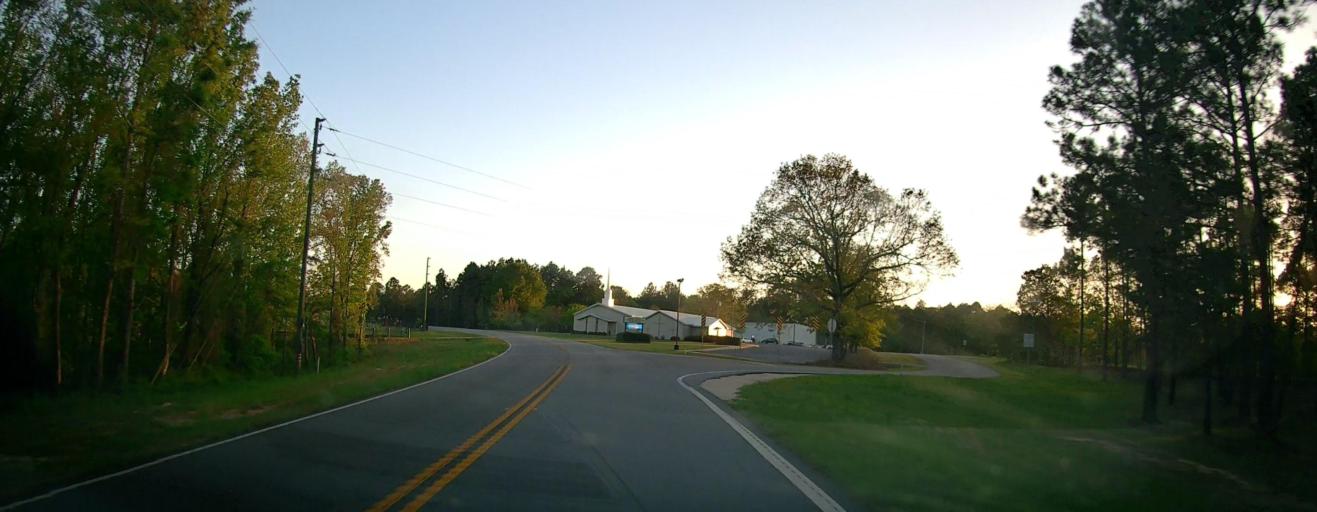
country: US
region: Georgia
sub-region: Marion County
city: Buena Vista
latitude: 32.4791
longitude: -84.6350
